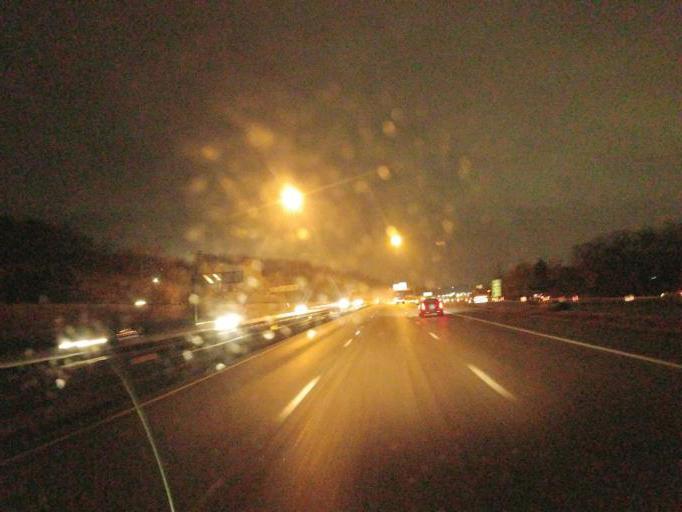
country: US
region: Missouri
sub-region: Saint Louis County
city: Sunset Hills
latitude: 38.5473
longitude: -90.4284
